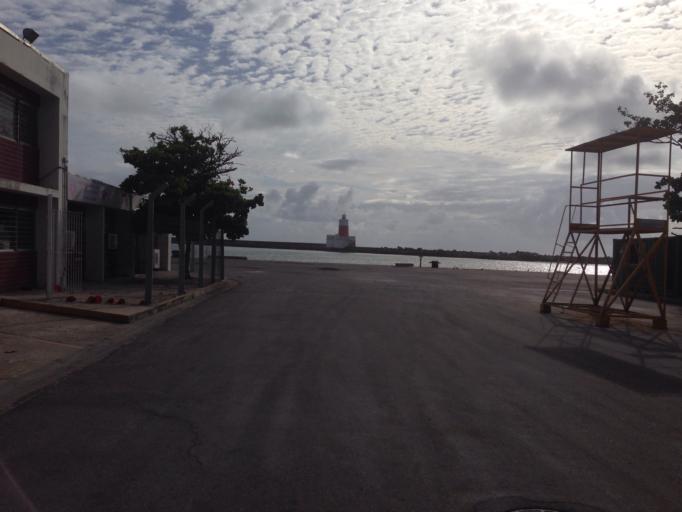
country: BR
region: Pernambuco
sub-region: Recife
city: Recife
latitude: -8.0546
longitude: -34.8684
